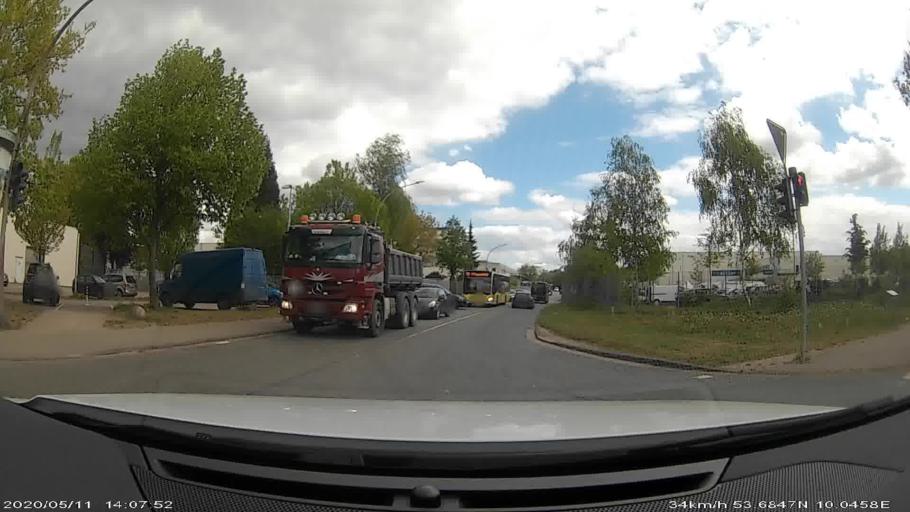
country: DE
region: Hamburg
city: Poppenbuettel
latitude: 53.6838
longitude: 10.0662
